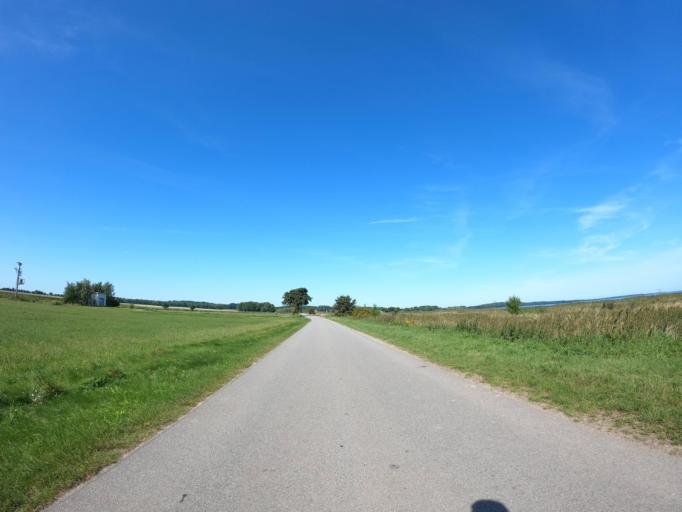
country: DE
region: Mecklenburg-Vorpommern
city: Prohn
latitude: 54.3924
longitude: 13.0289
